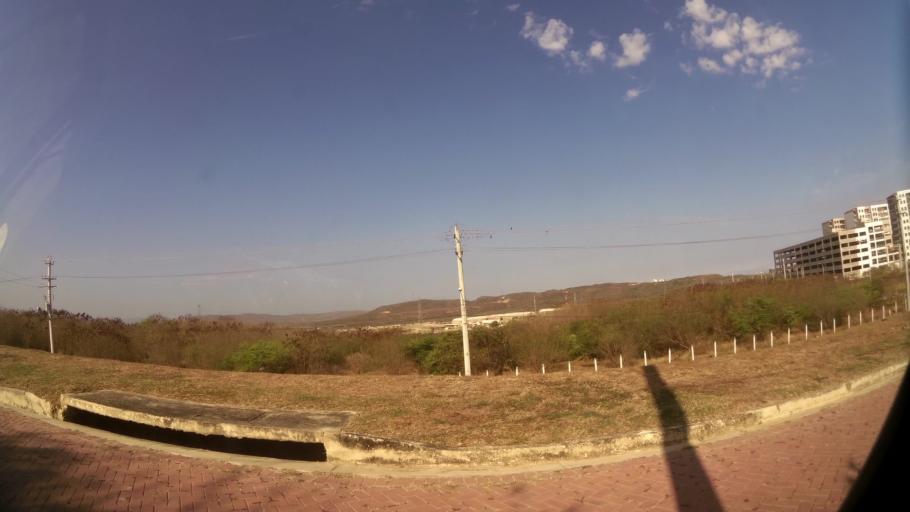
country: CO
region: Atlantico
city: Barranquilla
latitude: 11.0044
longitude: -74.8378
